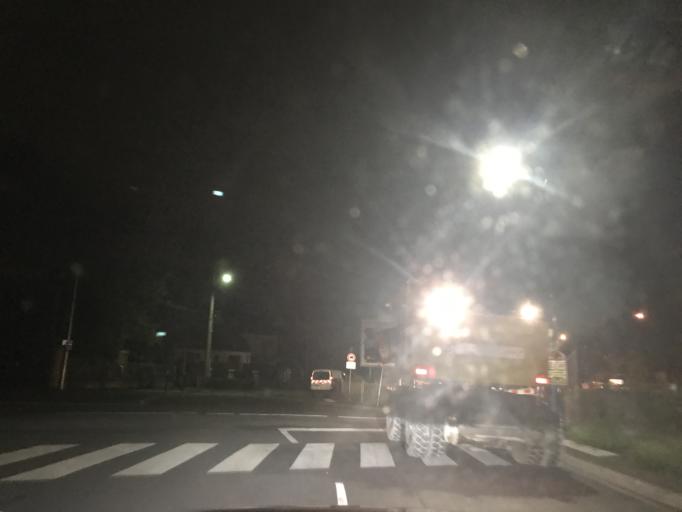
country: FR
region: Ile-de-France
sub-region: Departement des Yvelines
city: Sartrouville
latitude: 48.9391
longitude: 2.1922
